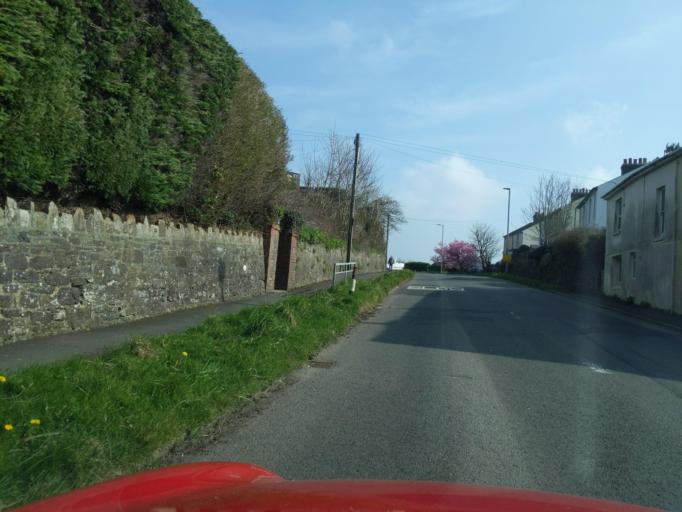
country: GB
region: England
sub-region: Devon
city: Ivybridge
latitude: 50.3972
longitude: -3.8767
